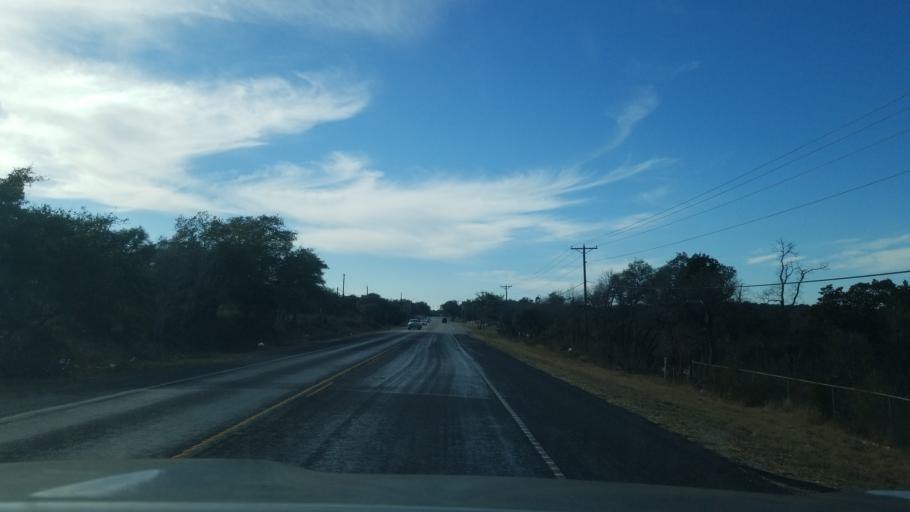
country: US
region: Texas
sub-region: Comal County
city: Canyon Lake
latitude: 29.7733
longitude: -98.2853
